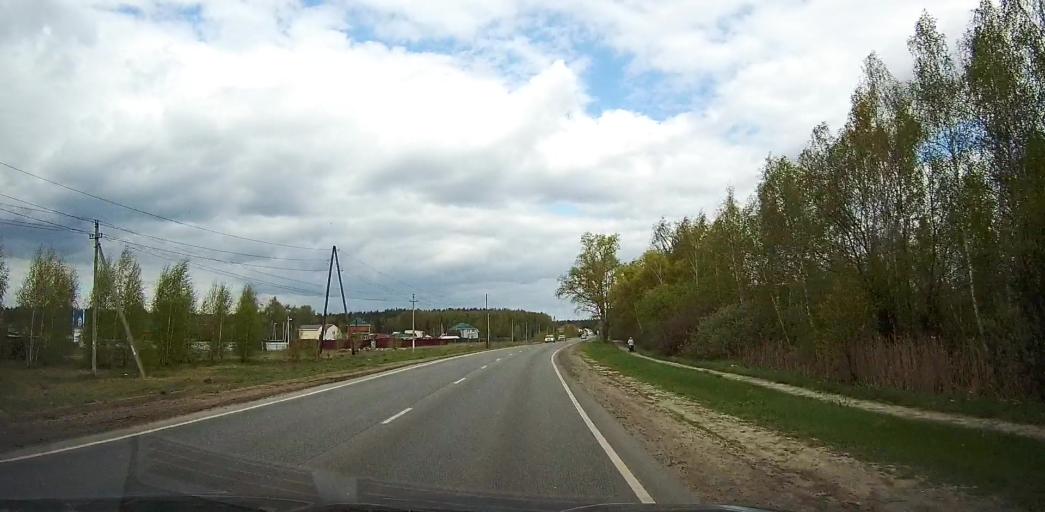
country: RU
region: Moskovskaya
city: Ashitkovo
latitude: 55.4304
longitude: 38.5782
